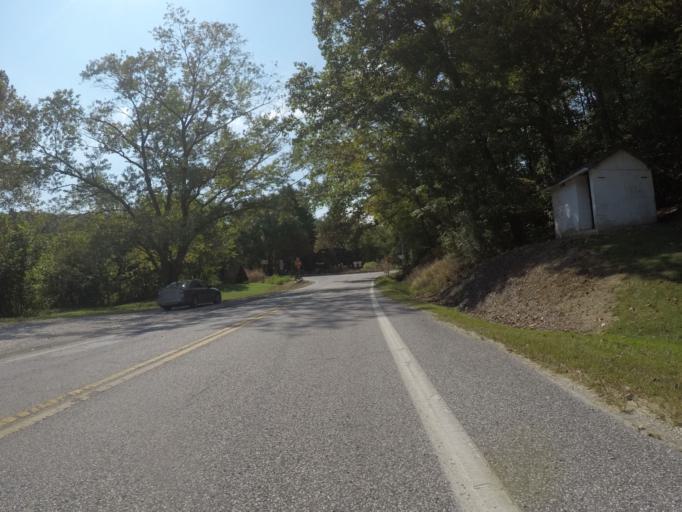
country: US
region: West Virginia
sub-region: Cabell County
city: Lesage
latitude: 38.5510
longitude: -82.3907
